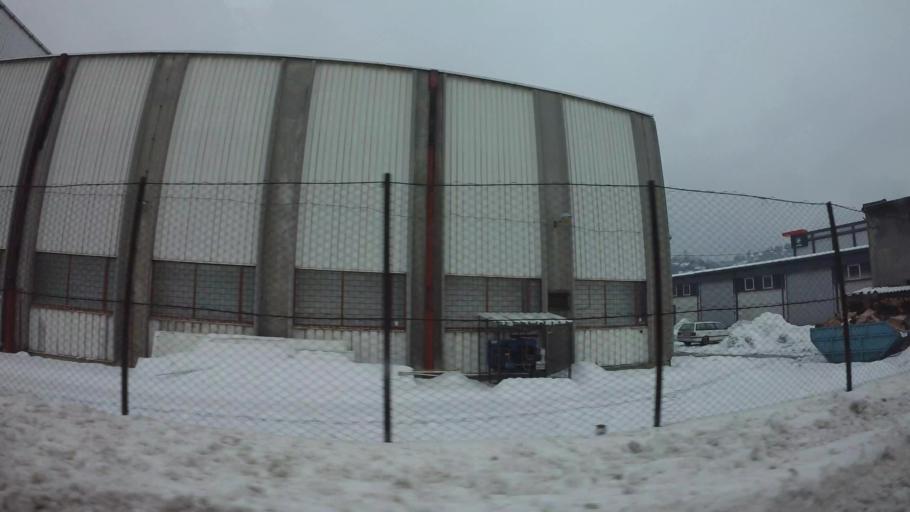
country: BA
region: Federation of Bosnia and Herzegovina
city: Hadzici
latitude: 43.8393
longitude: 18.2603
